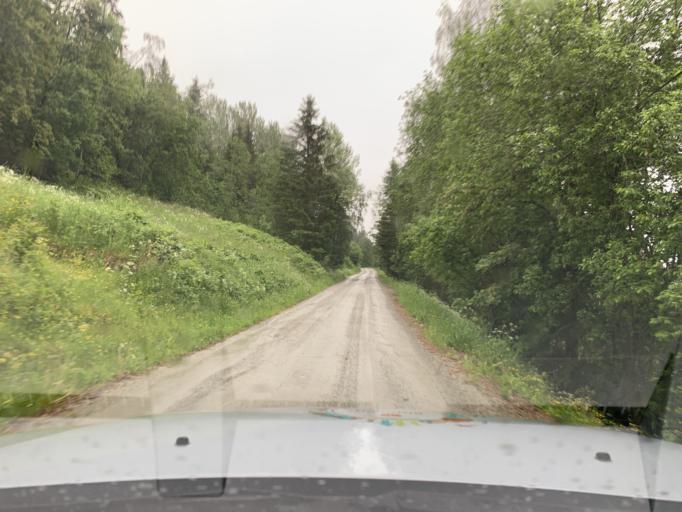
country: NO
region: Oppland
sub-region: Oyer
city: Tretten
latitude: 61.3918
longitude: 10.2756
